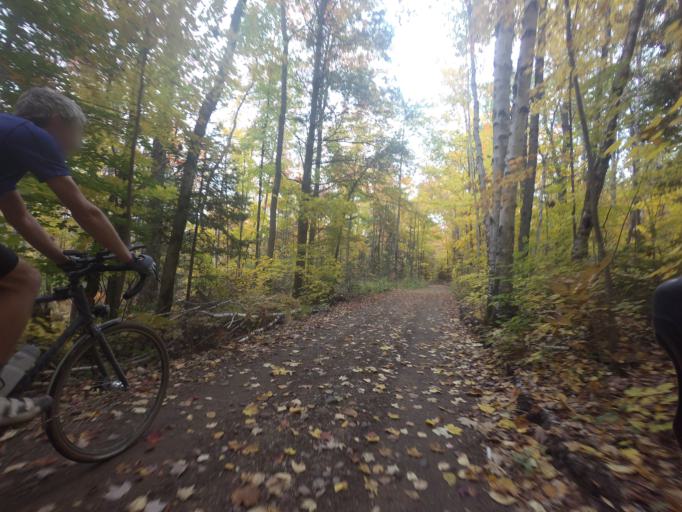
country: CA
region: Ontario
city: Pembroke
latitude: 45.7257
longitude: -77.2265
